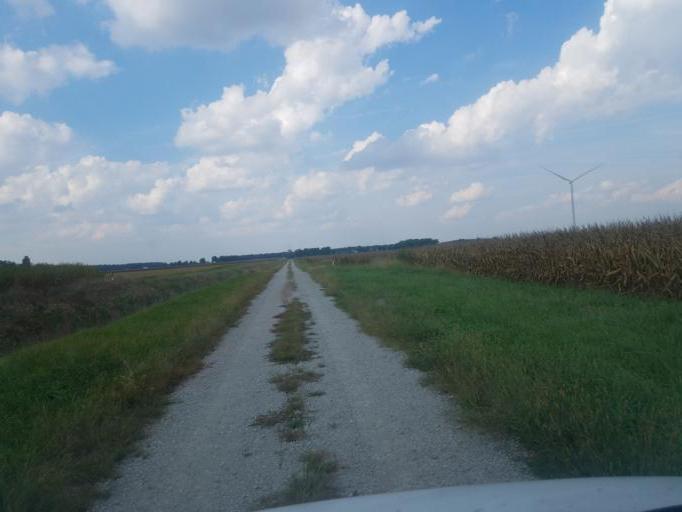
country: US
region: Ohio
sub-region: Hancock County
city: Arlington
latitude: 40.7975
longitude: -83.6898
